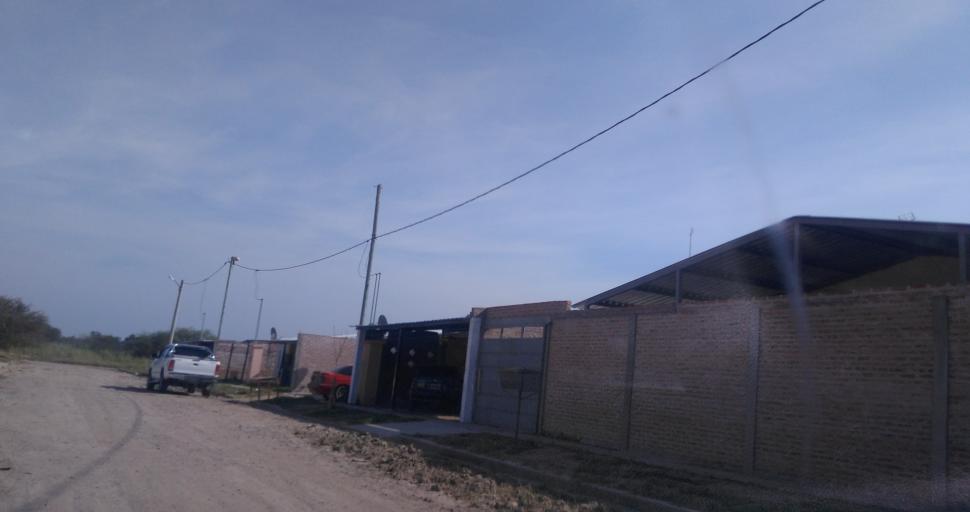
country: AR
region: Chaco
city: Fontana
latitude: -27.4564
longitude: -59.0507
